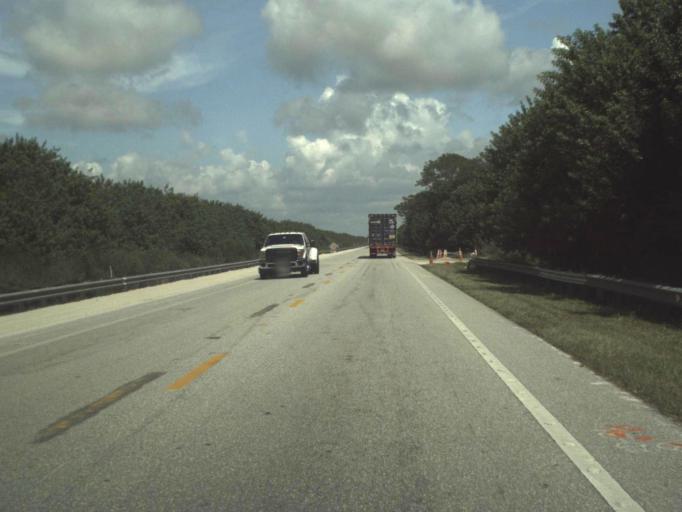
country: US
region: Florida
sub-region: Okeechobee County
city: Taylor Creek
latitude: 27.1346
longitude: -80.6404
